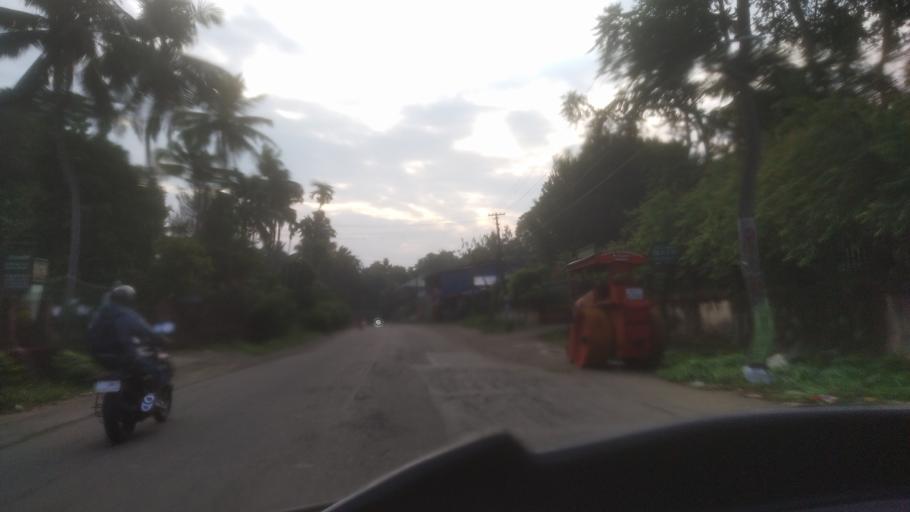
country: IN
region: Kerala
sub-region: Ernakulam
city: Kotamangalam
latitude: 10.0932
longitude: 76.5600
